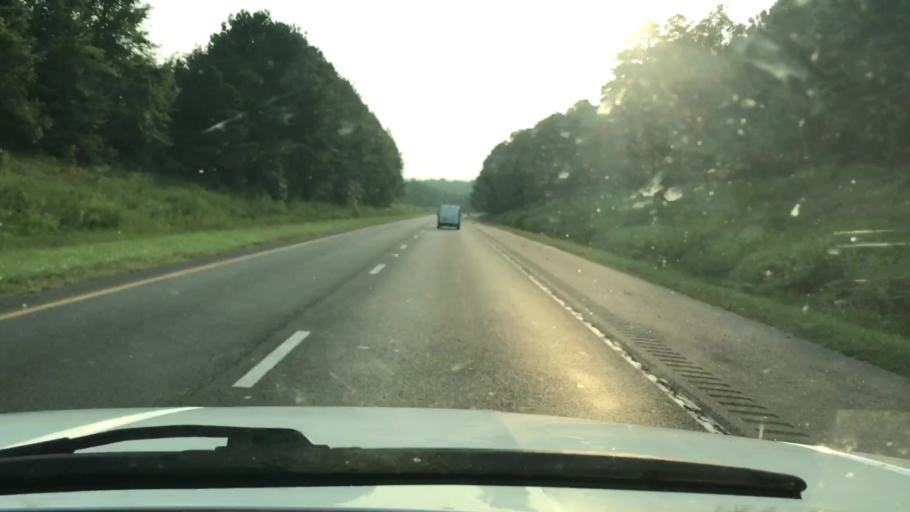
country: US
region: Virginia
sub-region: Chesterfield County
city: Brandermill
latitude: 37.4103
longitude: -77.6057
